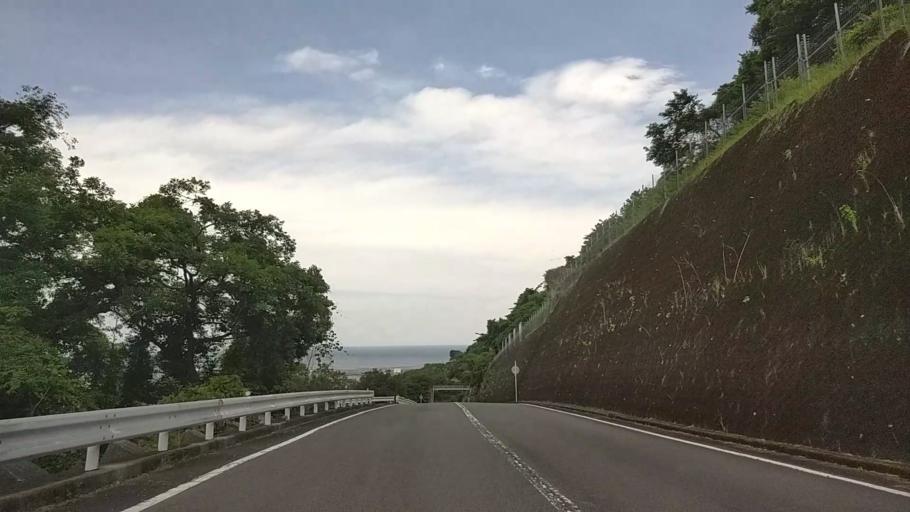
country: JP
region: Kanagawa
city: Odawara
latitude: 35.2433
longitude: 139.1337
